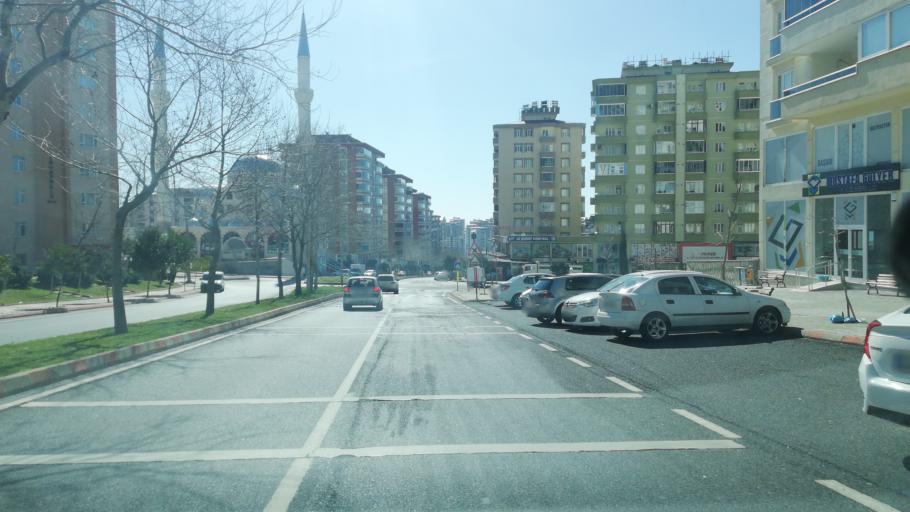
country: TR
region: Kahramanmaras
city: Kahramanmaras
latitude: 37.5877
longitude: 36.8783
